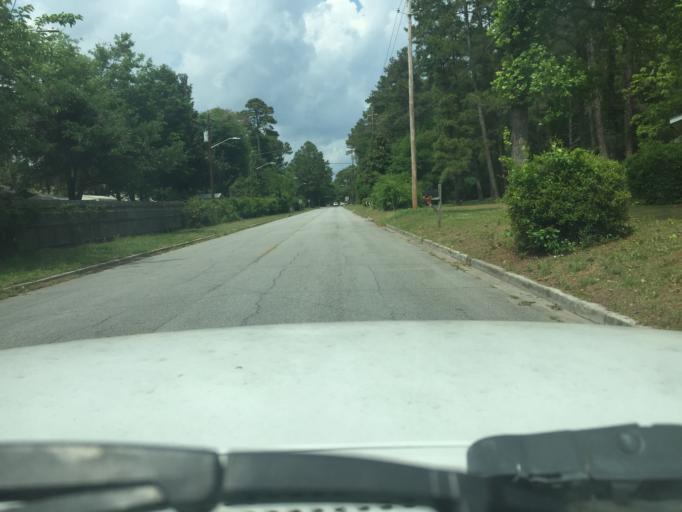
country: US
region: Georgia
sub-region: Chatham County
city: Isle of Hope
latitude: 32.0023
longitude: -81.0725
